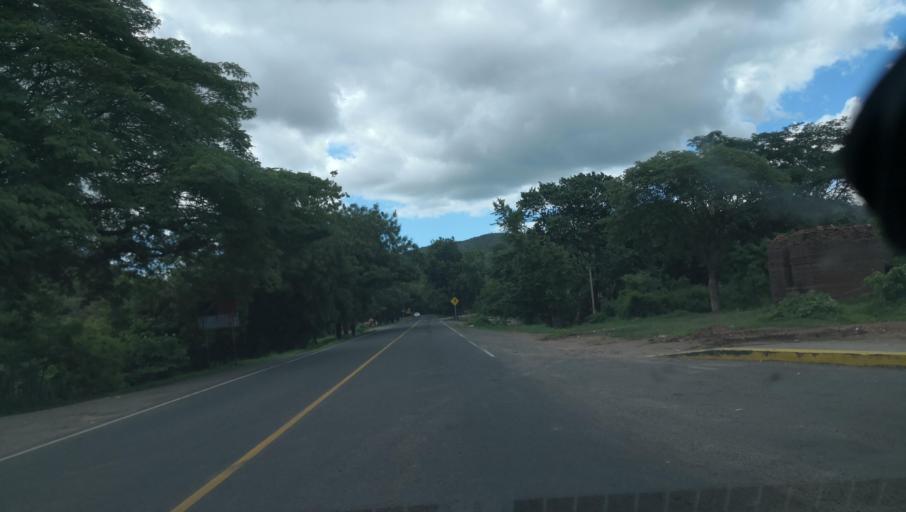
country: NI
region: Madriz
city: Palacaguina
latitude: 13.4548
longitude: -86.4513
